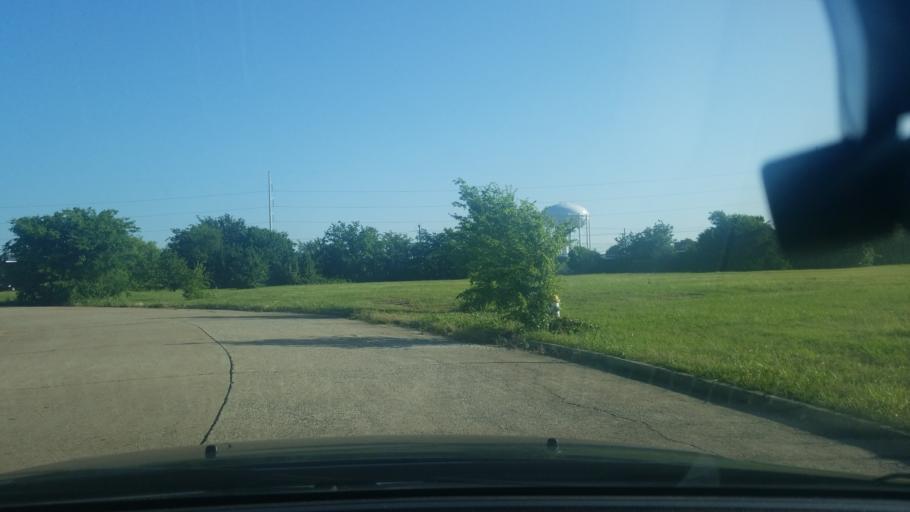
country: US
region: Texas
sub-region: Dallas County
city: Mesquite
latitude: 32.7906
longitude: -96.6721
